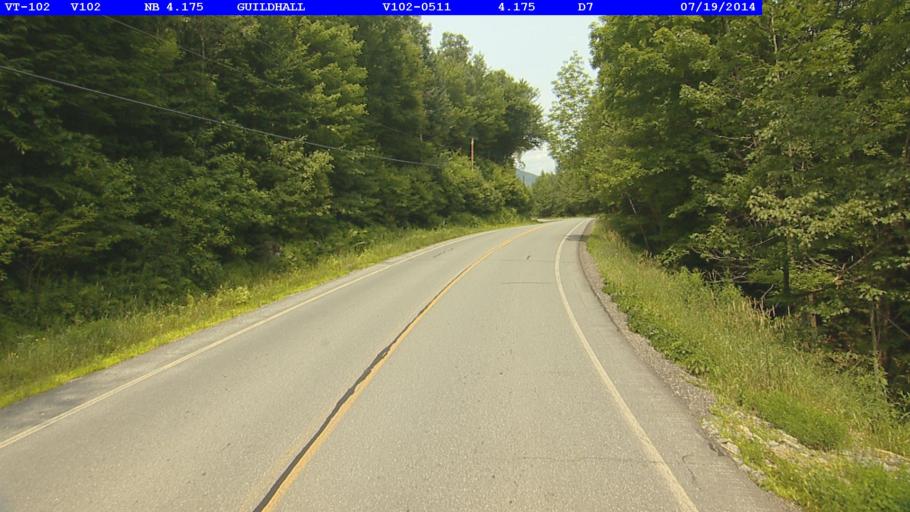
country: US
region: Vermont
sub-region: Essex County
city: Guildhall
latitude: 44.5495
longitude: -71.5917
